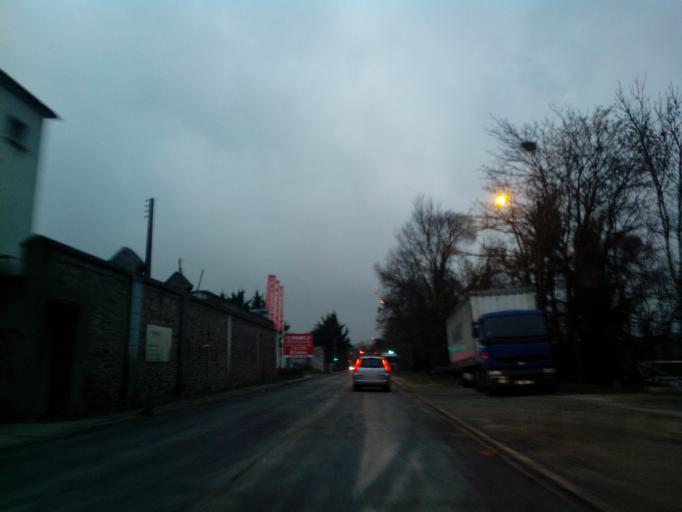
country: FR
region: Ile-de-France
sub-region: Departement de l'Essonne
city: Saint-Germain-les-Corbeil
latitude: 48.6201
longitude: 2.4749
